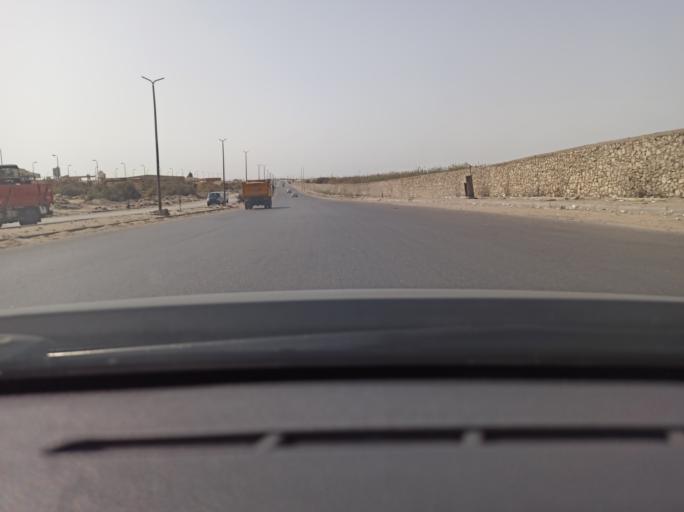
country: EG
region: Muhafazat al Qahirah
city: Halwan
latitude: 29.8158
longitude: 31.3514
